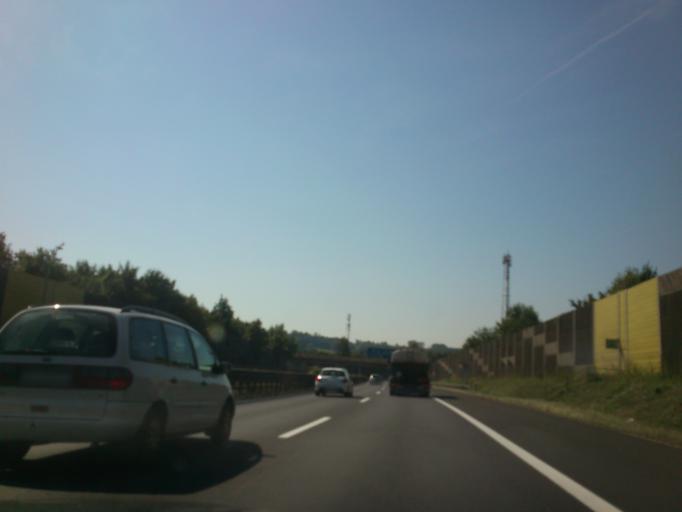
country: AT
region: Upper Austria
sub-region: Politischer Bezirk Linz-Land
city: Ansfelden
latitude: 48.2288
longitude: 14.2982
